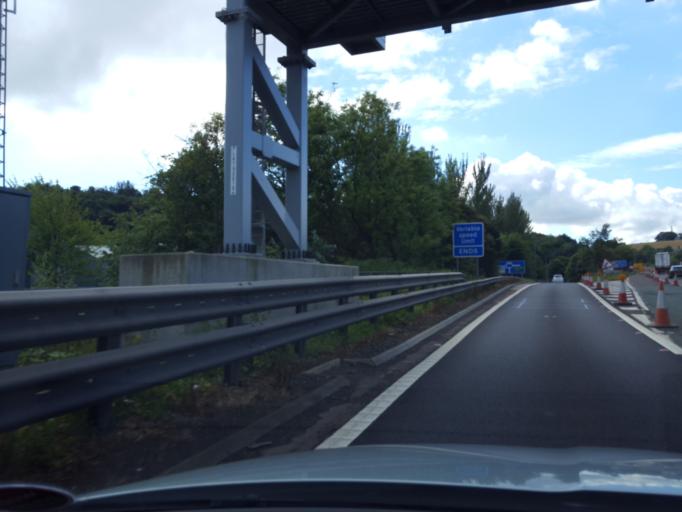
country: GB
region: Scotland
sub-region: Fife
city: Inverkeithing
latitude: 56.0386
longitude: -3.4068
